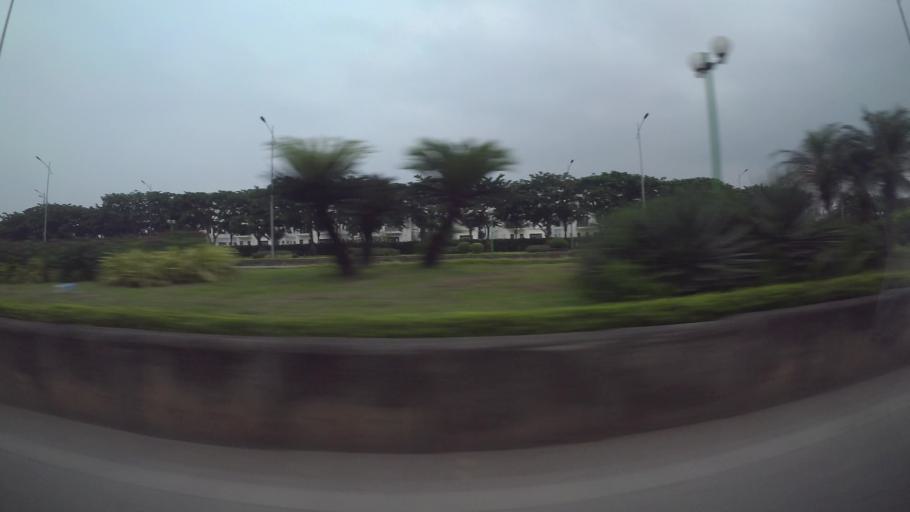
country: VN
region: Ha Noi
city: Trau Quy
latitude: 21.0459
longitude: 105.9081
